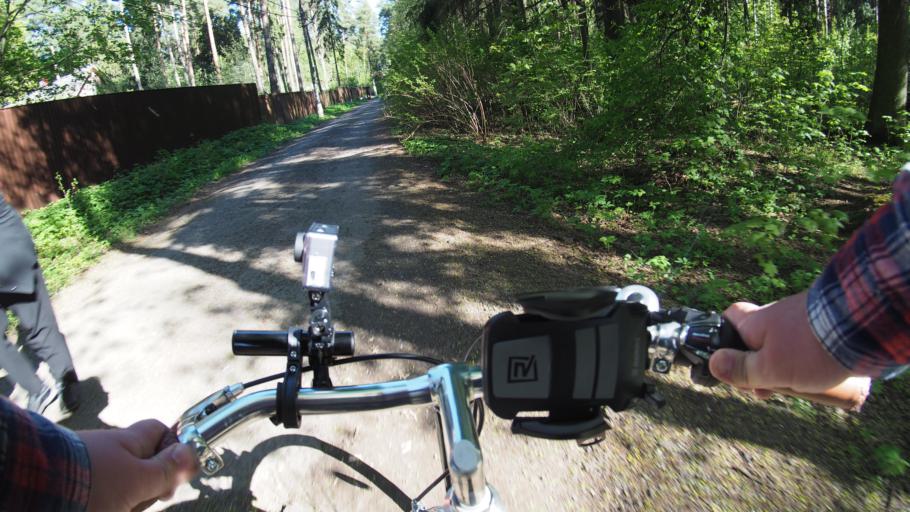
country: RU
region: Moskovskaya
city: Kratovo
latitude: 55.5816
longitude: 38.1771
